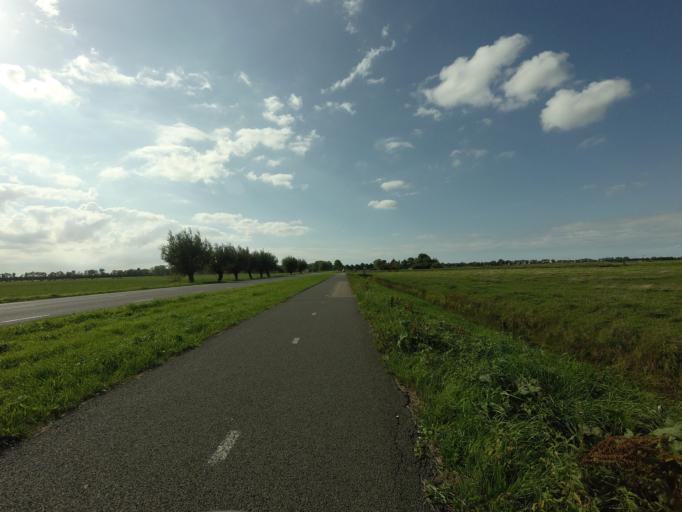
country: NL
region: Friesland
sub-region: Sudwest Fryslan
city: Bolsward
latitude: 53.0587
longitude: 5.5495
